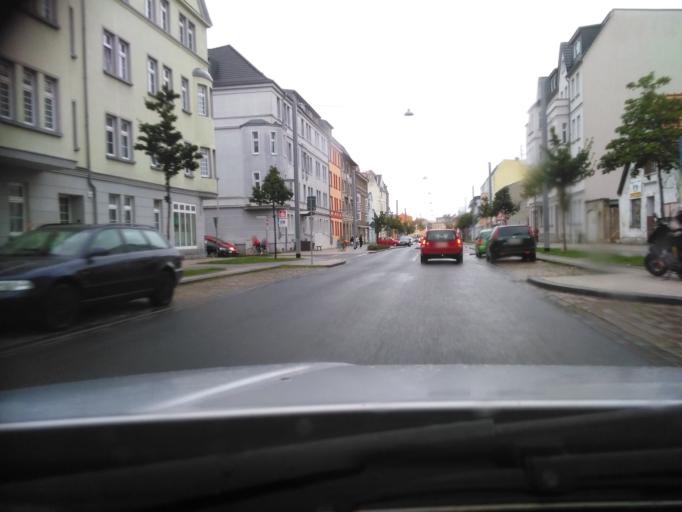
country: DE
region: Mecklenburg-Vorpommern
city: Stralsund
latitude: 54.3048
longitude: 13.0971
